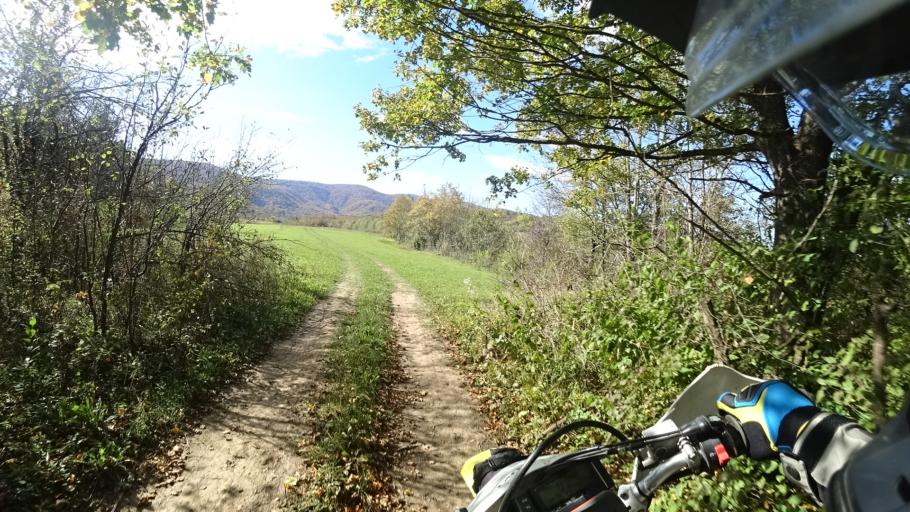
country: HR
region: Karlovacka
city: Plaski
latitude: 45.0924
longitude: 15.3496
